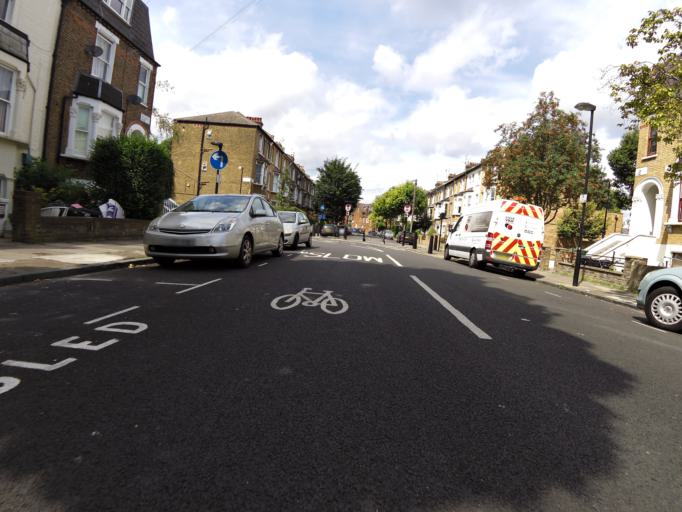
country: GB
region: England
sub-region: Greater London
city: Holloway
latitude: 51.5580
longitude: -0.1305
